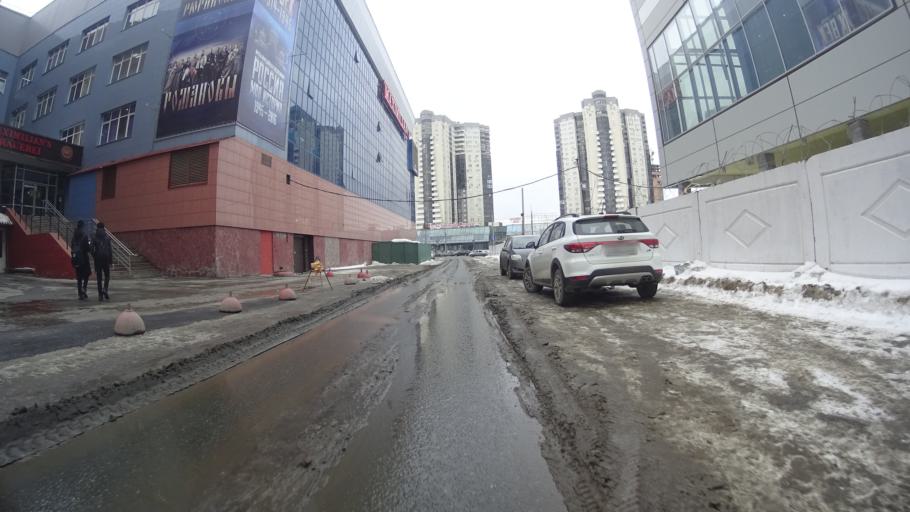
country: RU
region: Chelyabinsk
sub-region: Gorod Chelyabinsk
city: Chelyabinsk
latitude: 55.1681
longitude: 61.3756
